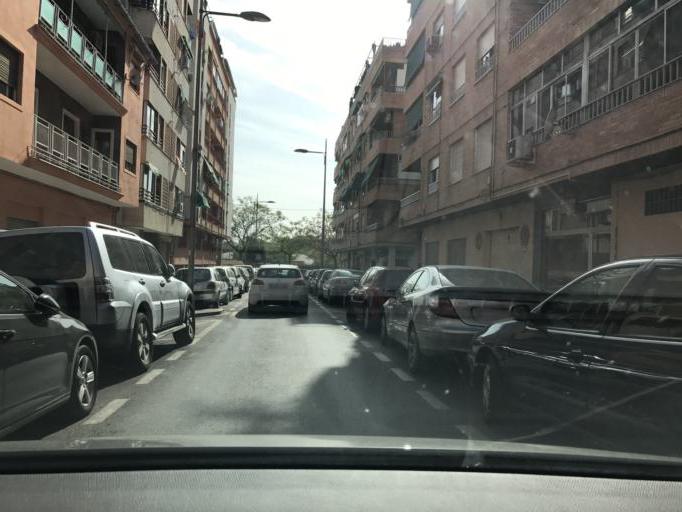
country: ES
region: Andalusia
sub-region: Provincia de Granada
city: Granada
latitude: 37.1856
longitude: -3.6111
